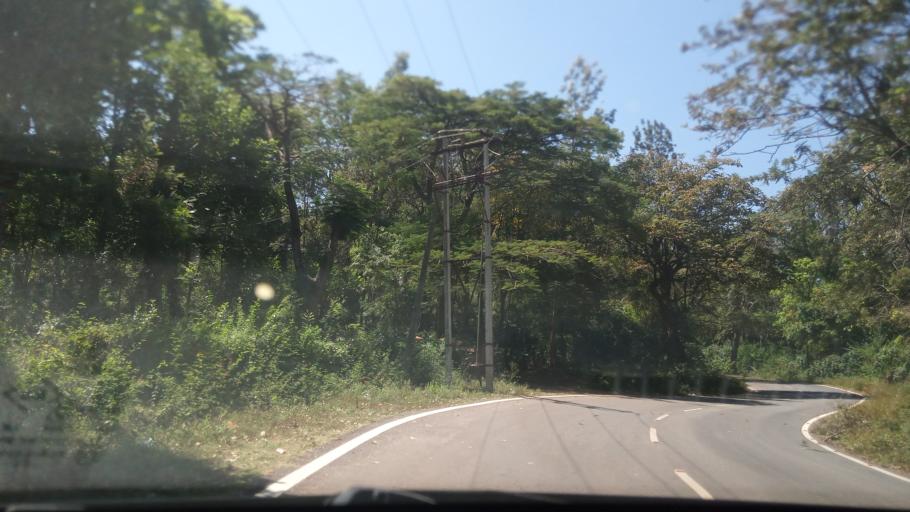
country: IN
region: Karnataka
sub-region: Chikmagalur
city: Chikmagalur
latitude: 13.4643
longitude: 75.7987
